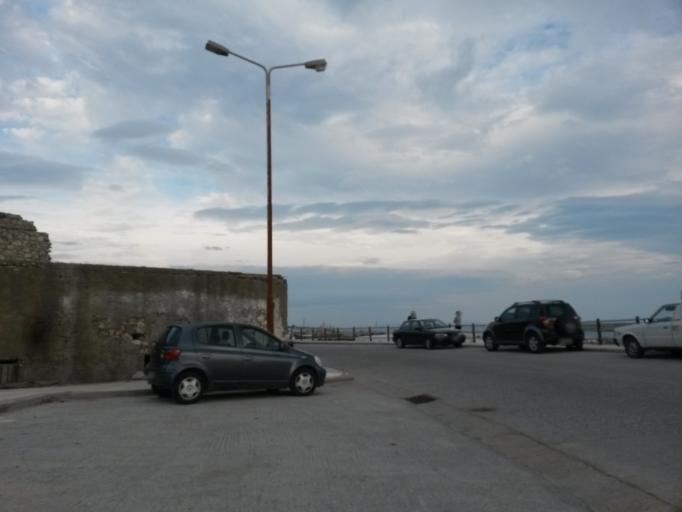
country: GR
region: North Aegean
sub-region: Nomos Lesvou
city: Plomarion
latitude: 38.9748
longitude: 26.3672
